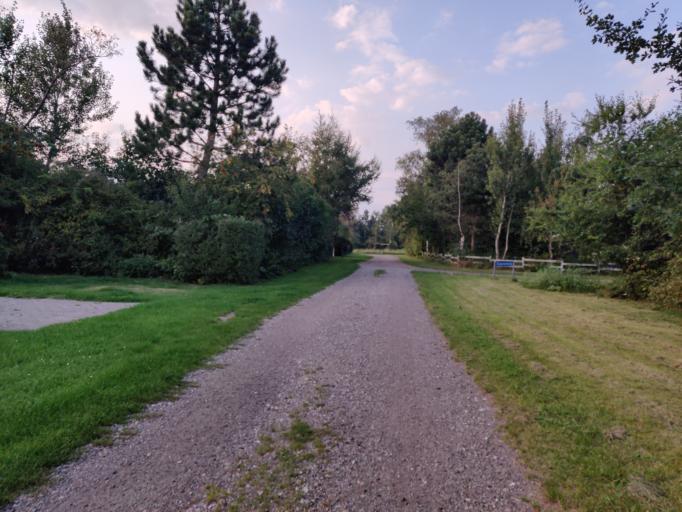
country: DK
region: Zealand
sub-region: Guldborgsund Kommune
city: Nykobing Falster
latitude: 54.5893
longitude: 11.9665
